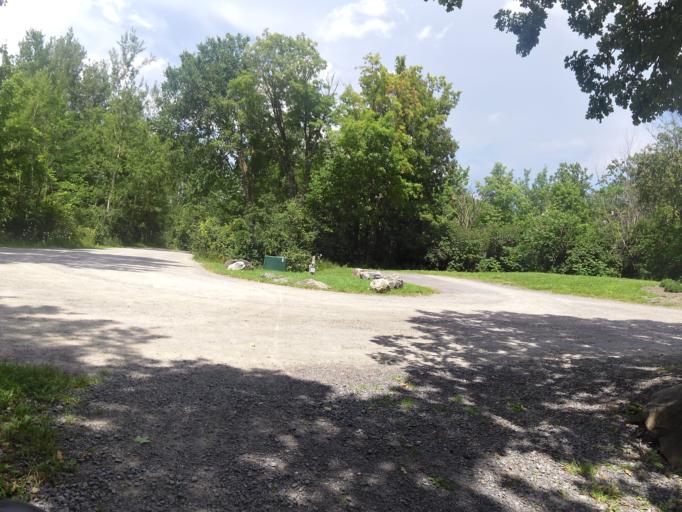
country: CA
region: Ontario
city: Bells Corners
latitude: 45.3173
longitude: -75.9221
